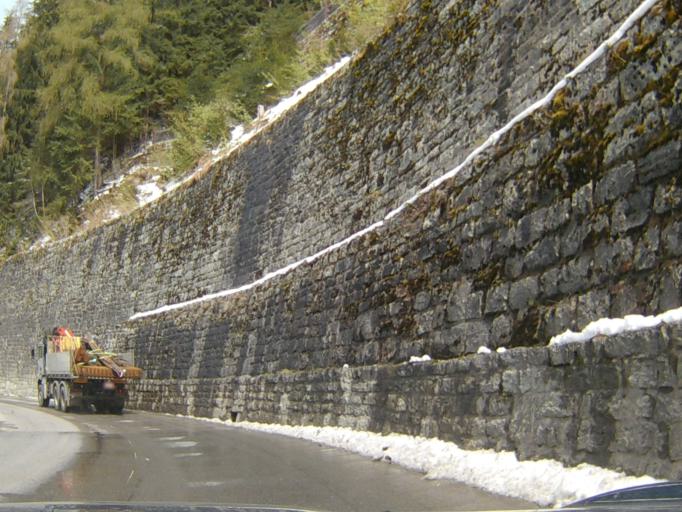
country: AT
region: Tyrol
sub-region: Politischer Bezirk Schwaz
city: Gerlosberg
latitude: 47.2107
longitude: 11.9402
